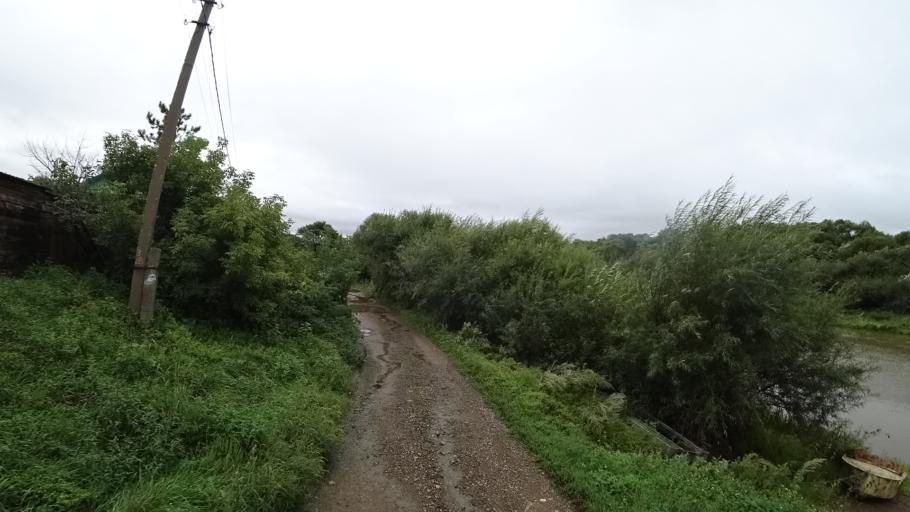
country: RU
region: Primorskiy
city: Monastyrishche
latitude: 44.2733
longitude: 132.4057
